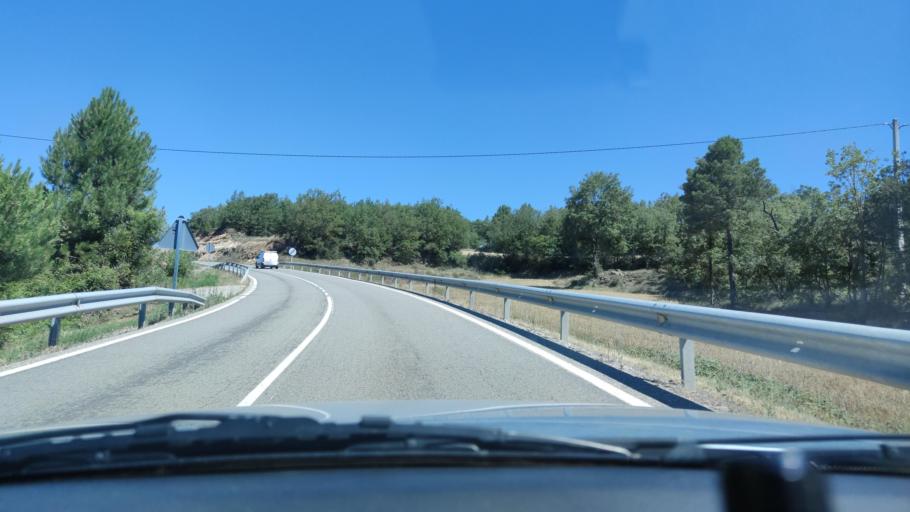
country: ES
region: Catalonia
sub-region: Provincia de Lleida
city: Solsona
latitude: 41.9045
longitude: 1.5359
